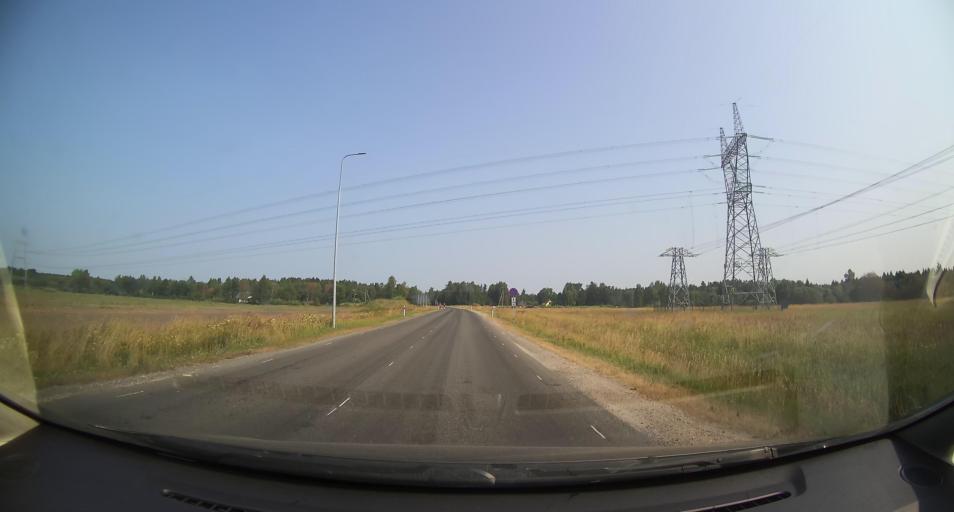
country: EE
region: Paernumaa
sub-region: Audru vald
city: Audru
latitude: 58.4236
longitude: 24.3151
